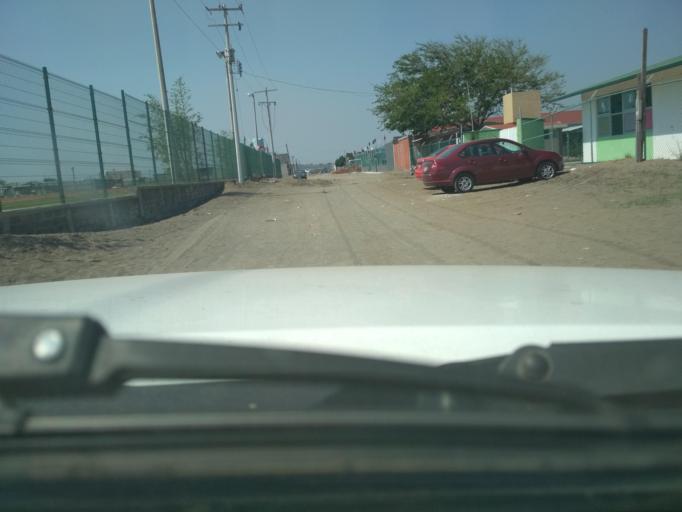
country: MX
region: Veracruz
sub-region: Veracruz
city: Lomas de Rio Medio Cuatro
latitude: 19.1933
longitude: -96.1983
